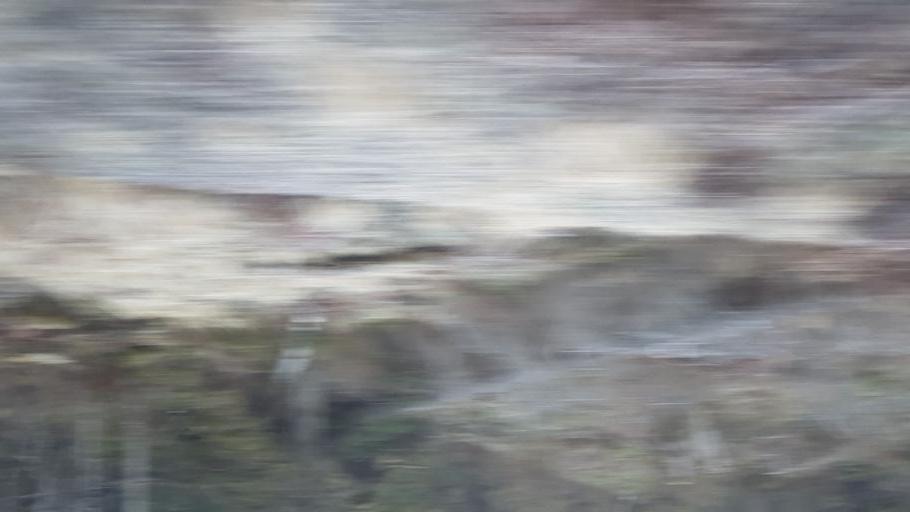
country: NO
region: Nord-Trondelag
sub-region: Stjordal
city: Stjordalshalsen
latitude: 63.5858
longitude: 11.0062
